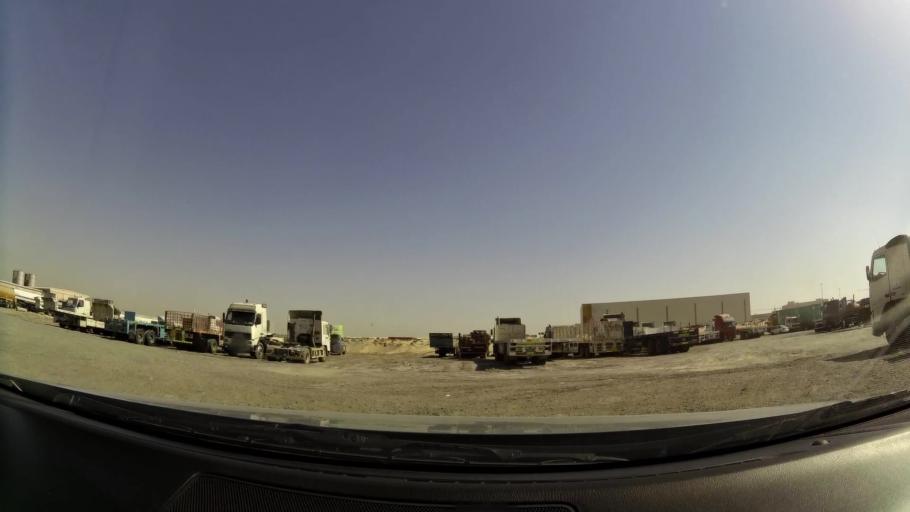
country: AE
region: Dubai
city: Dubai
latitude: 25.0056
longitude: 55.1137
